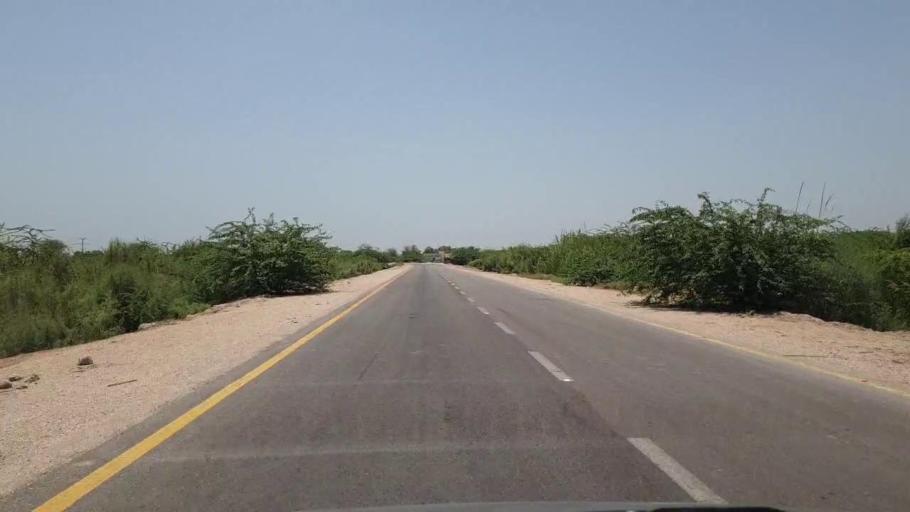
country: PK
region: Sindh
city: Sakrand
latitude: 26.1124
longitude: 68.3883
